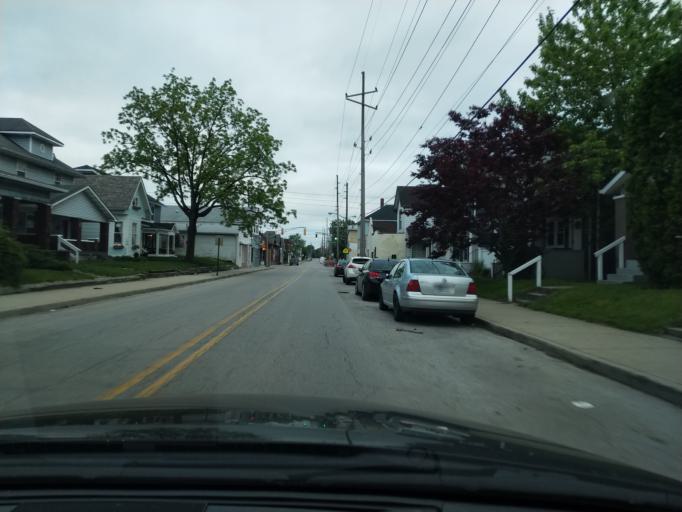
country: US
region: Indiana
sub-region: Marion County
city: Indianapolis
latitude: 39.7464
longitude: -86.1495
